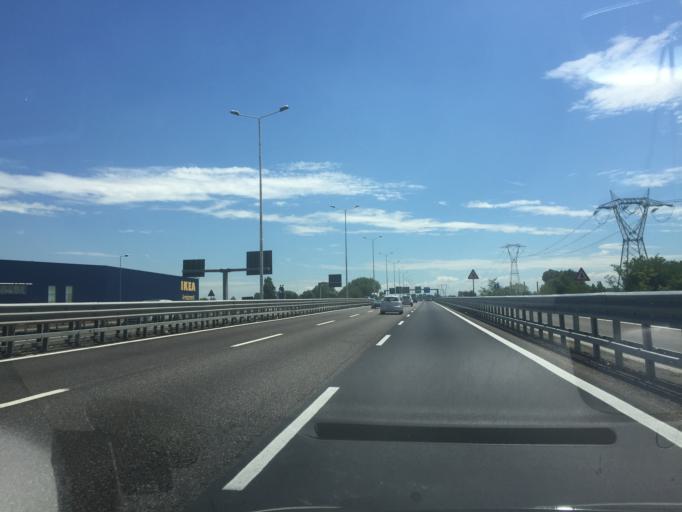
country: IT
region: Lombardy
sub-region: Citta metropolitana di Milano
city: Trezzano sul Naviglio
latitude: 45.4276
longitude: 9.0769
